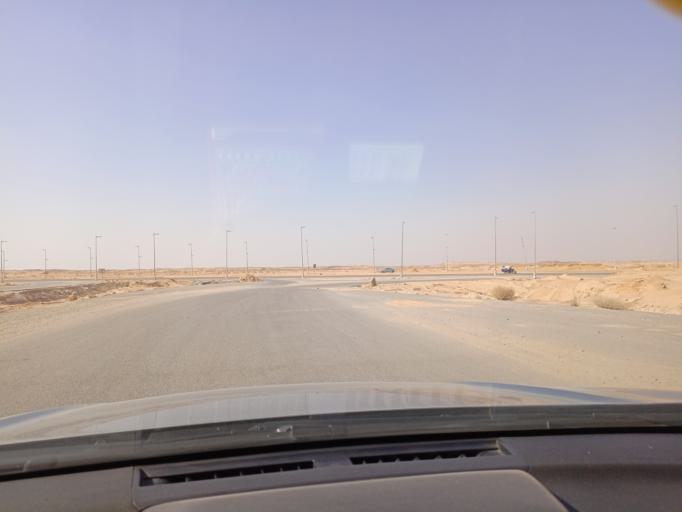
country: EG
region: Muhafazat al Qalyubiyah
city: Al Khankah
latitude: 30.0429
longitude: 31.7133
